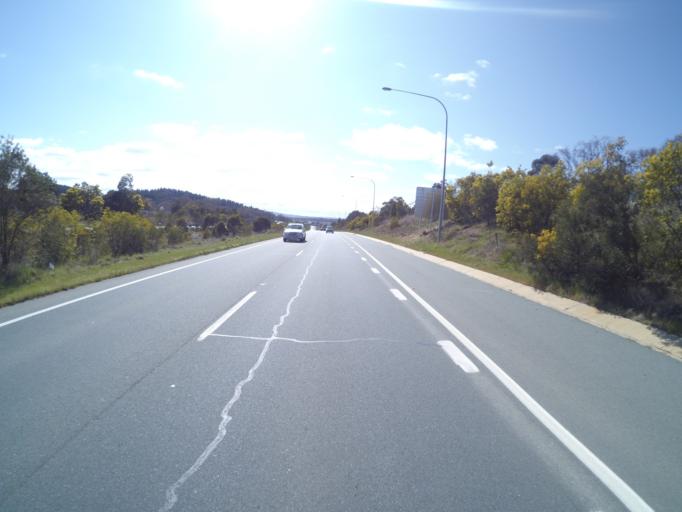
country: AU
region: Australian Capital Territory
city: Kaleen
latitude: -35.2046
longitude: 149.2045
